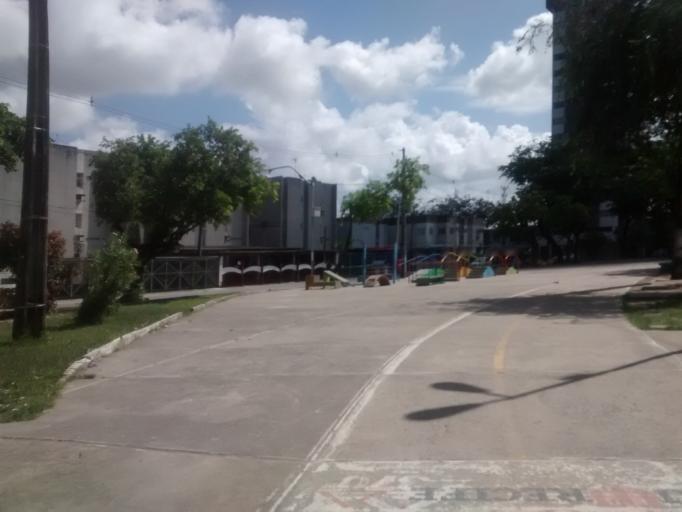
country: BR
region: Pernambuco
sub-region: Recife
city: Recife
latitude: -8.0966
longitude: -34.9147
